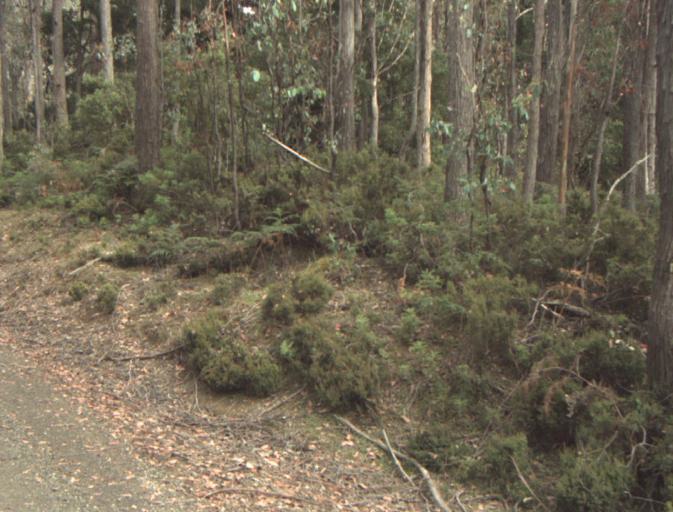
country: AU
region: Tasmania
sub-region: Northern Midlands
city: Evandale
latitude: -41.4989
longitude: 147.5804
